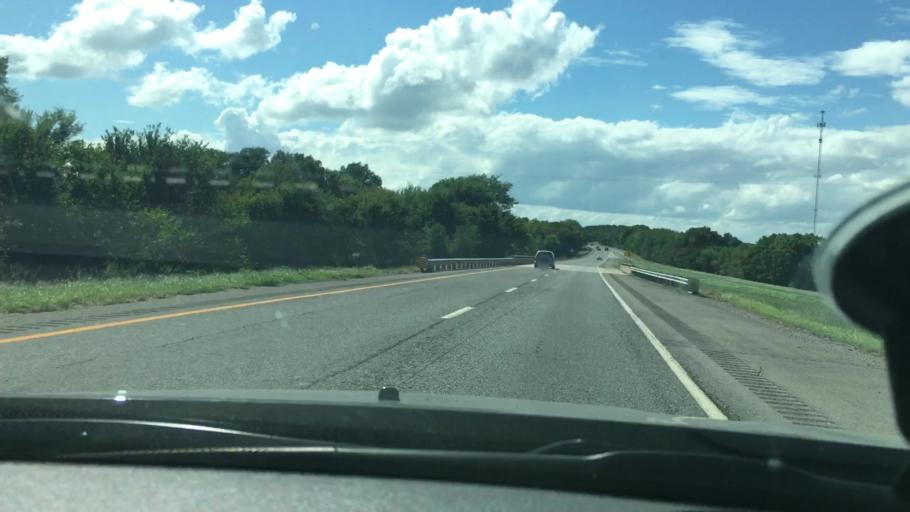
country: US
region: Oklahoma
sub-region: Sequoyah County
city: Vian
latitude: 35.4902
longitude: -95.0780
